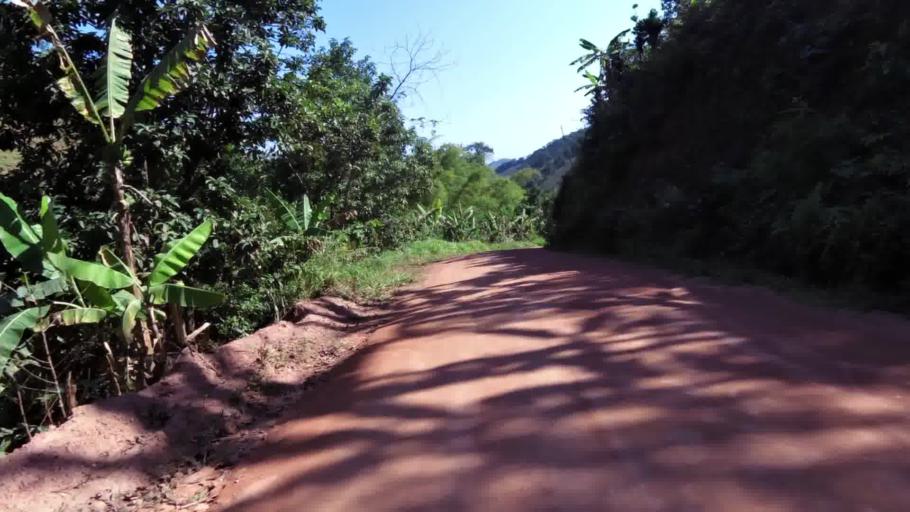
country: BR
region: Espirito Santo
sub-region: Alfredo Chaves
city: Alfredo Chaves
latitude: -20.5694
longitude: -40.7819
